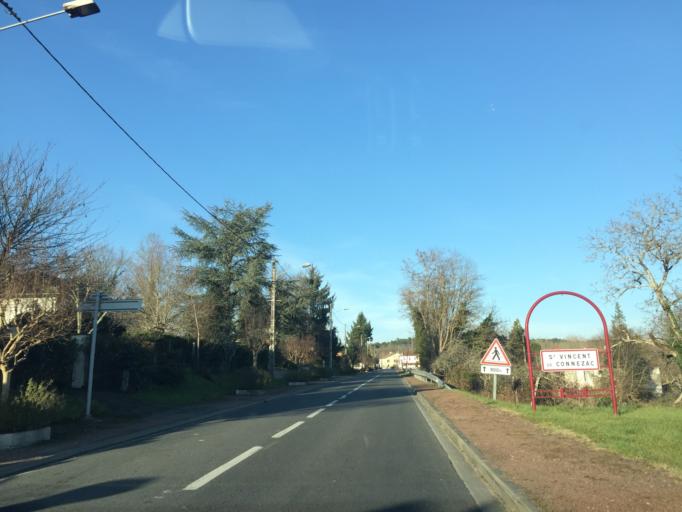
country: FR
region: Aquitaine
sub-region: Departement de la Dordogne
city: Neuvic
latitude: 45.1592
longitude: 0.3976
